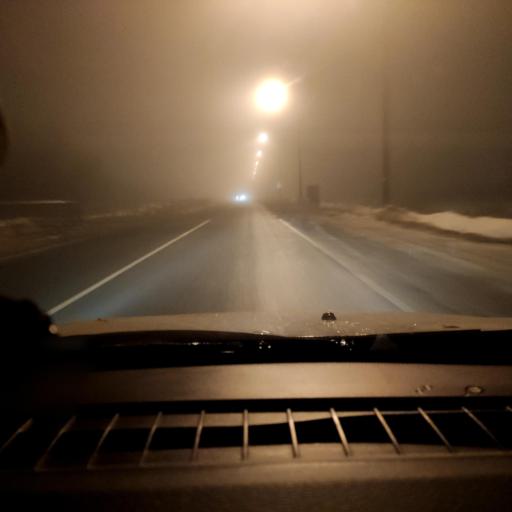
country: RU
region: Samara
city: Dubovyy Umet
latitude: 52.9728
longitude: 50.2763
